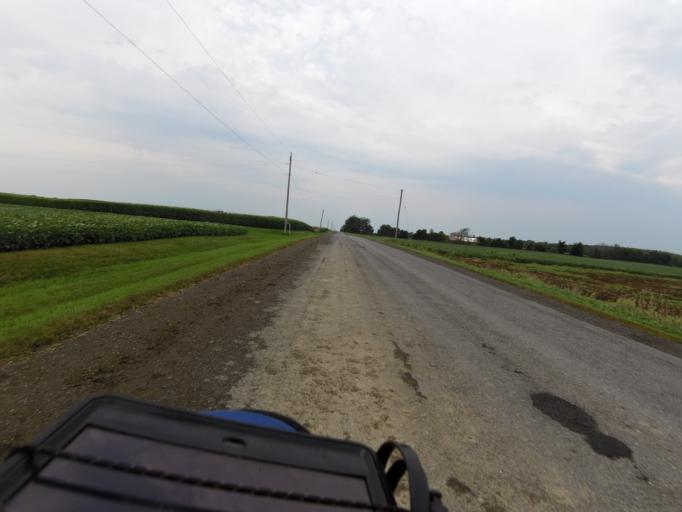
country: CA
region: Ontario
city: Casselman
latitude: 45.1681
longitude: -75.3604
